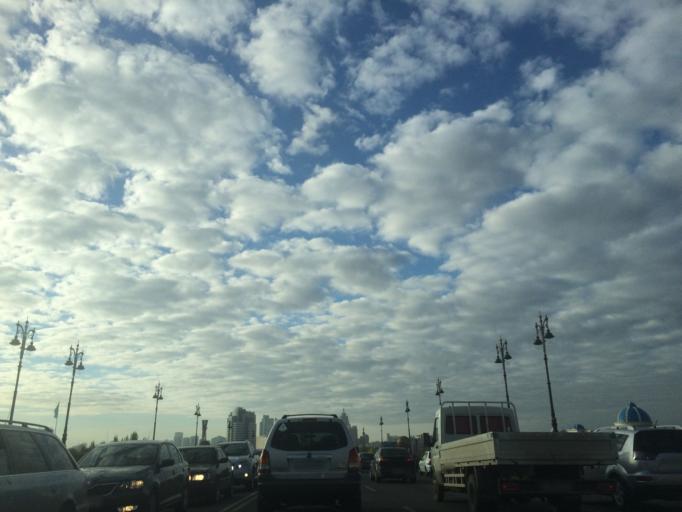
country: KZ
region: Astana Qalasy
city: Astana
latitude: 51.1578
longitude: 71.4113
